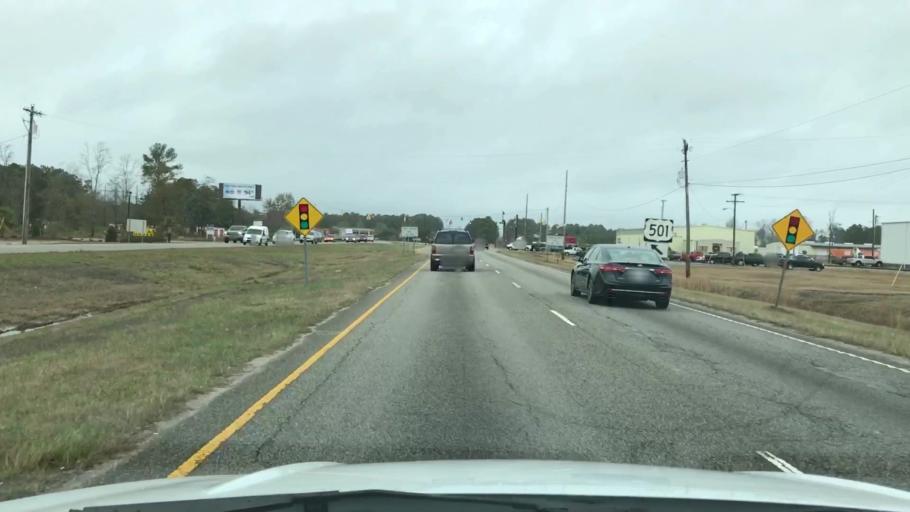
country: US
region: South Carolina
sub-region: Horry County
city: Red Hill
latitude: 33.8039
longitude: -79.0085
